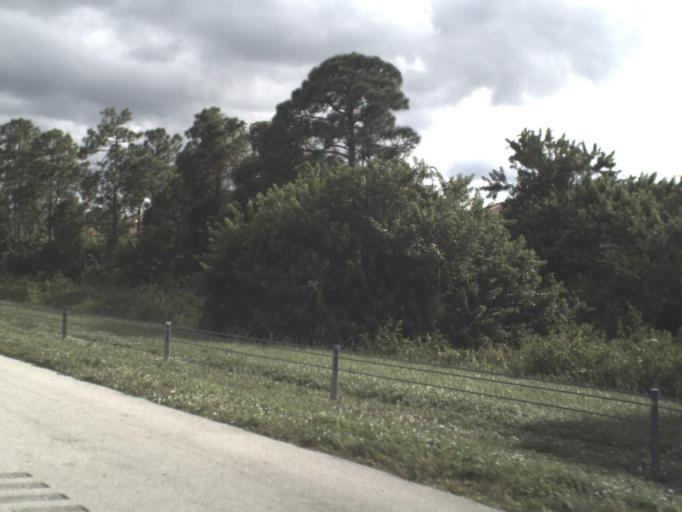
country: US
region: Florida
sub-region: Martin County
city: Palm City
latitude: 27.1075
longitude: -80.2678
